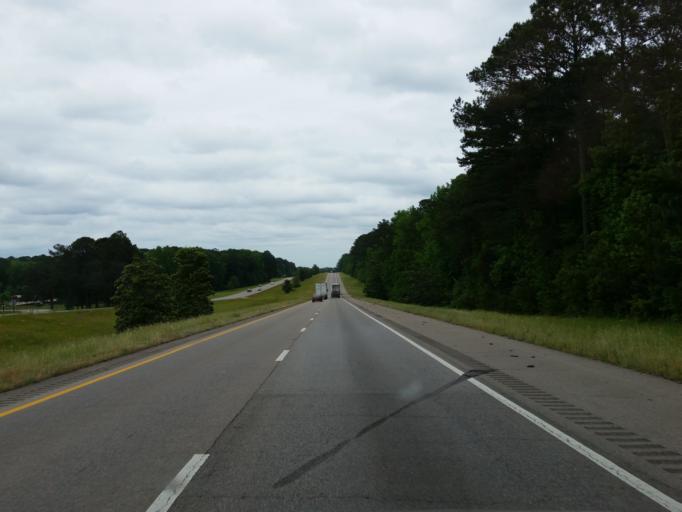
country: US
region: Mississippi
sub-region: Lauderdale County
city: Marion
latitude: 32.4082
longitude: -88.5387
